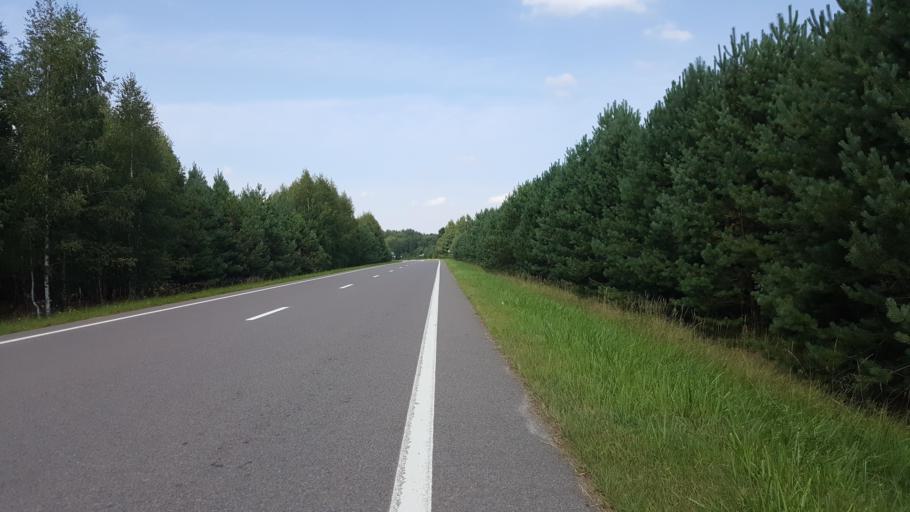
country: BY
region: Brest
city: Kamyanyuki
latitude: 52.5568
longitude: 23.6334
